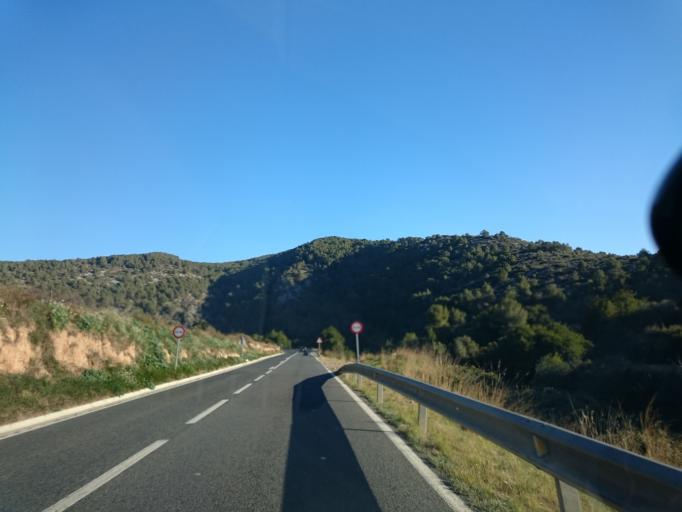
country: ES
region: Catalonia
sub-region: Provincia de Barcelona
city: Sant Pere de Ribes
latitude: 41.2694
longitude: 1.7665
